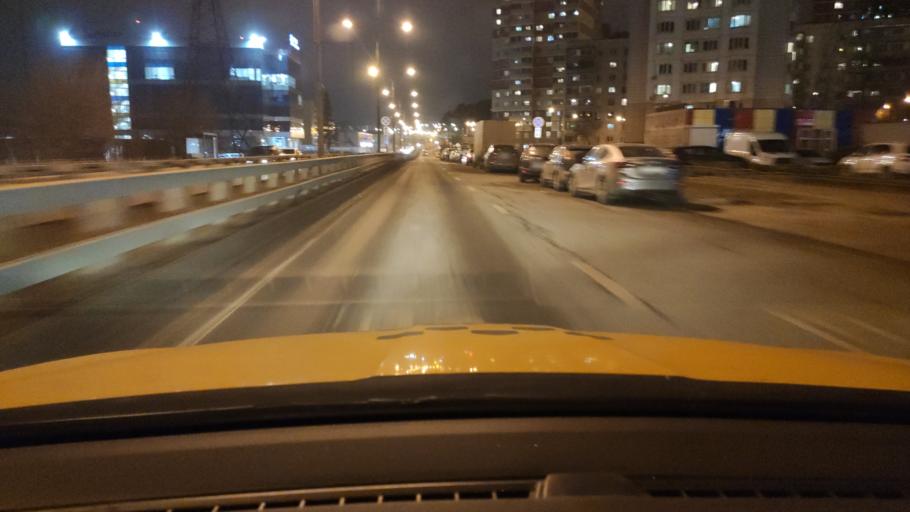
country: RU
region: Moskovskaya
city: Odintsovo
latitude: 55.6624
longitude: 37.2841
